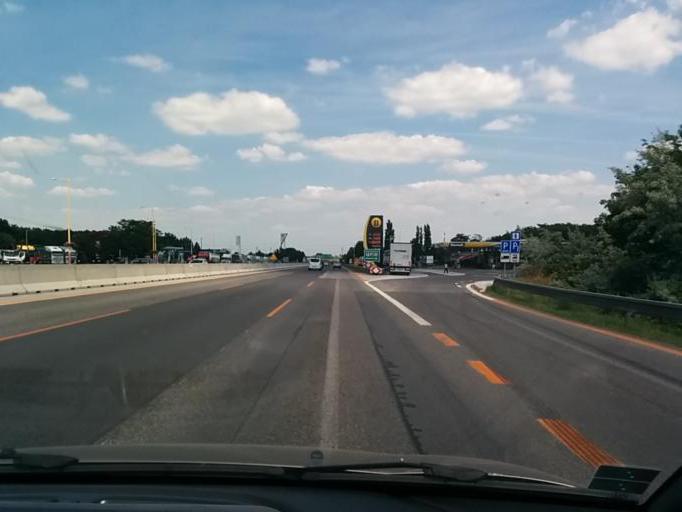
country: SK
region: Trnavsky
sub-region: Okres Trnava
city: Trnava
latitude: 48.3247
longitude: 17.6068
